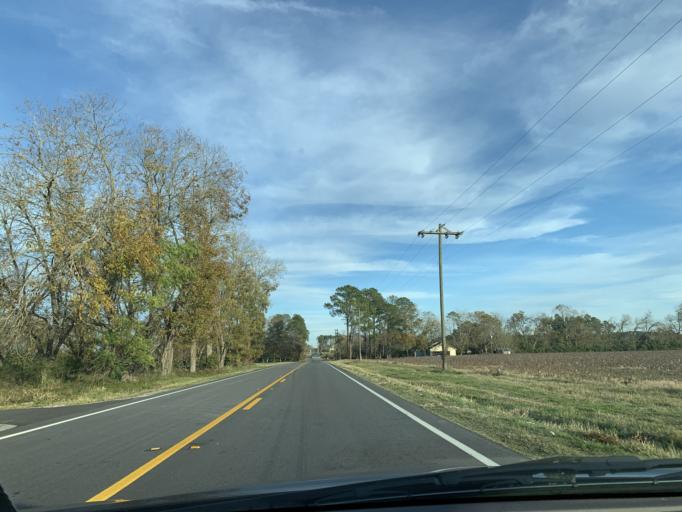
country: US
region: Georgia
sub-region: Irwin County
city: Ocilla
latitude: 31.5926
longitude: -83.2311
